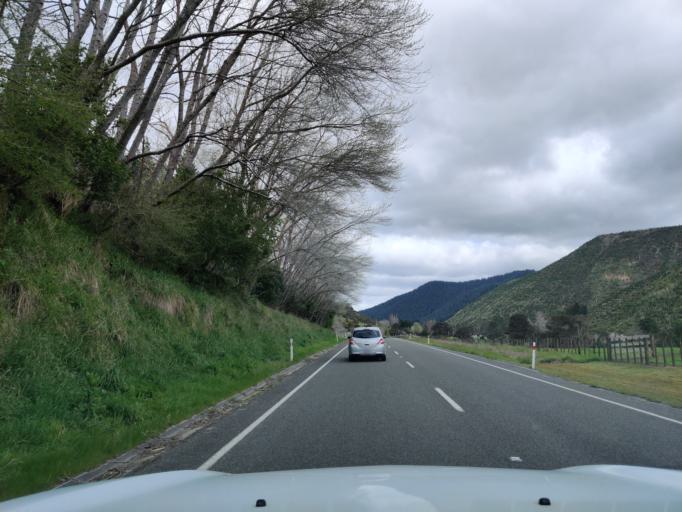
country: NZ
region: Manawatu-Wanganui
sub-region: Wanganui District
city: Wanganui
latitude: -39.8151
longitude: 175.1833
